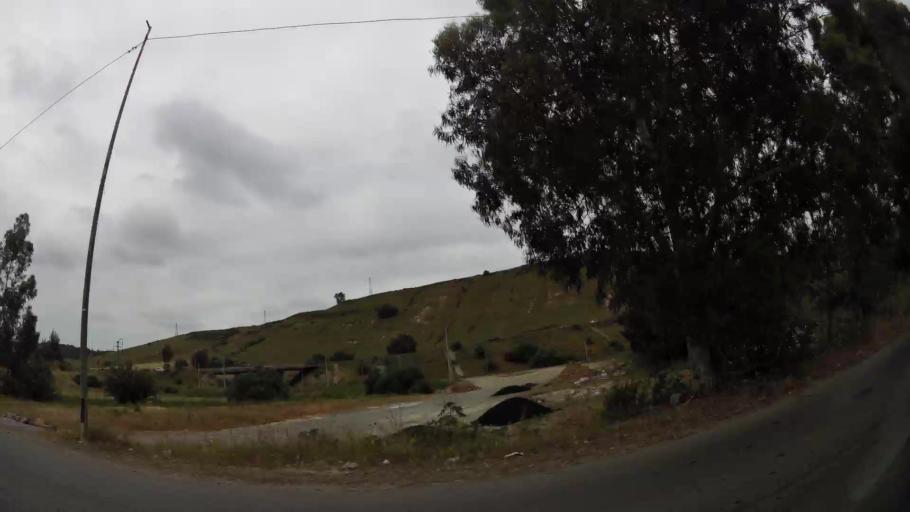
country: MA
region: Rabat-Sale-Zemmour-Zaer
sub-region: Rabat
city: Rabat
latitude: 33.9849
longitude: -6.7623
